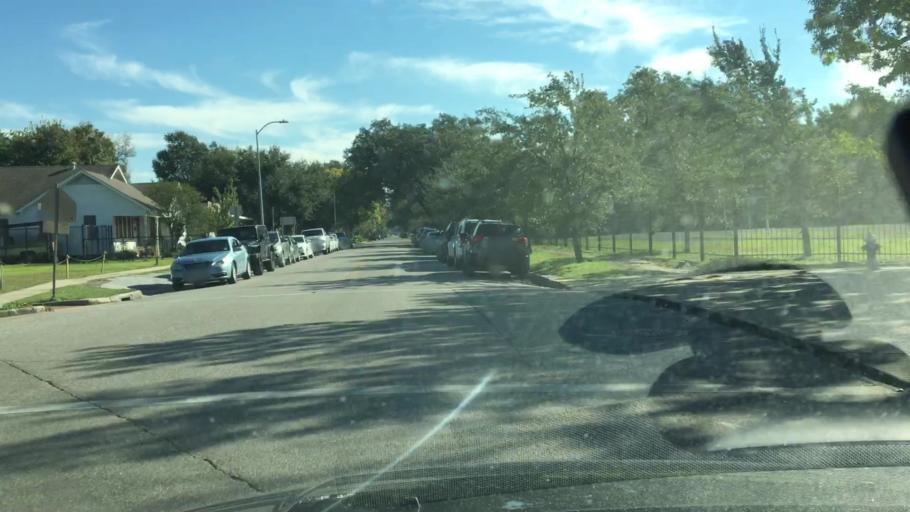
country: US
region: Texas
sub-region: Harris County
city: Houston
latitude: 29.7963
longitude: -95.3922
